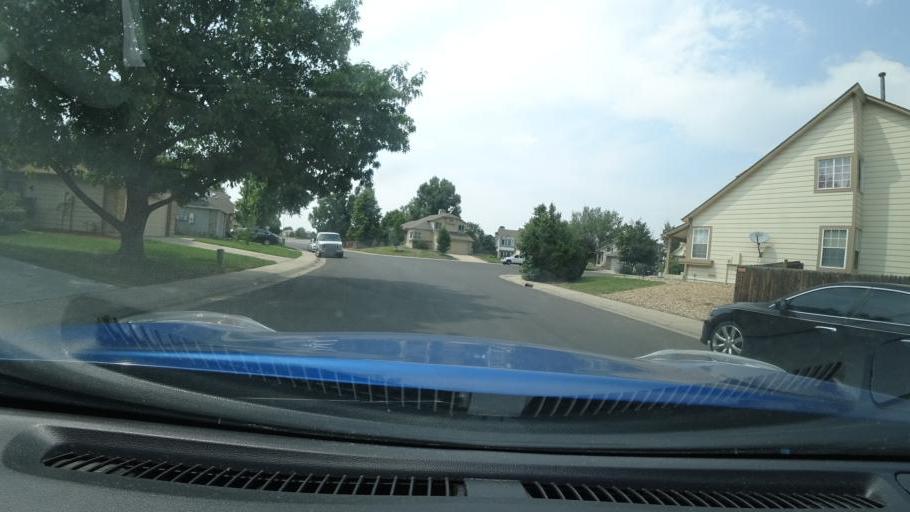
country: US
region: Colorado
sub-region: Adams County
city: Aurora
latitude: 39.7791
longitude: -104.7479
